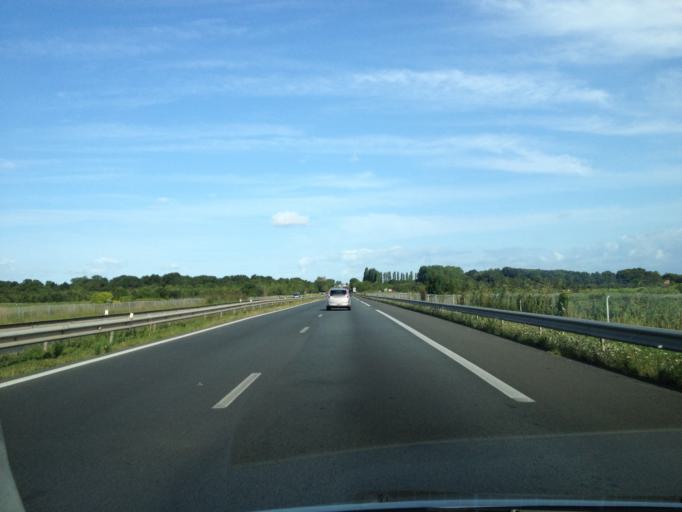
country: FR
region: Poitou-Charentes
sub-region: Departement de la Charente-Maritime
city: Saint-Laurent-de-la-Pree
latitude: 45.9838
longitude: -1.0216
